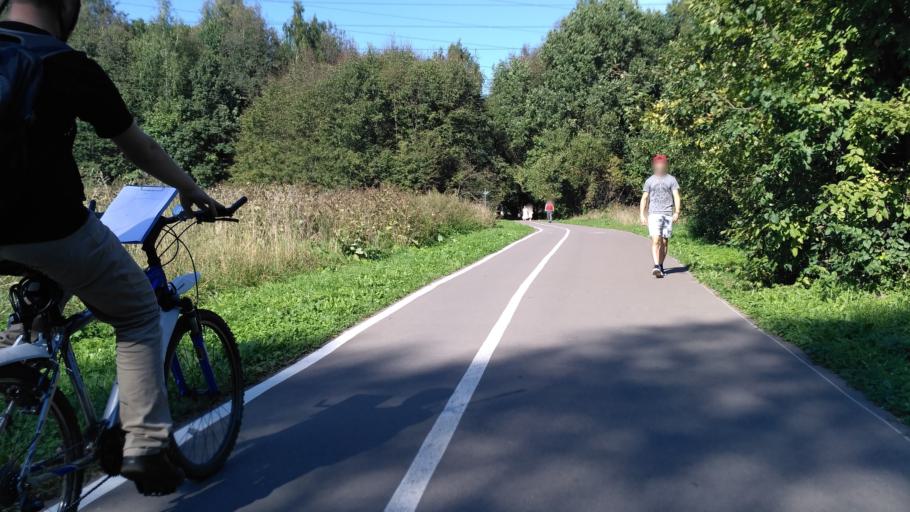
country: RU
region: Moskovskaya
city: Izmaylovo
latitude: 55.7802
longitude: 37.7766
